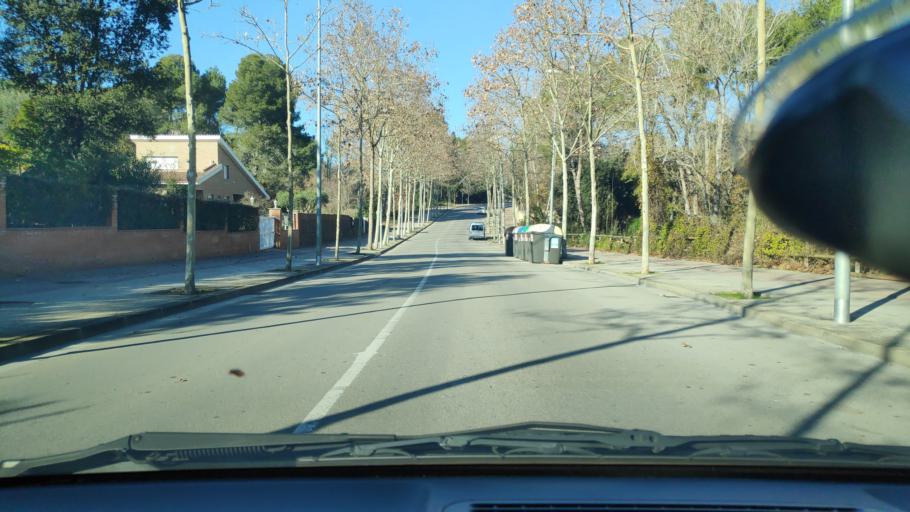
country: ES
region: Catalonia
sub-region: Provincia de Barcelona
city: Sant Quirze del Valles
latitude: 41.5606
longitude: 2.0746
